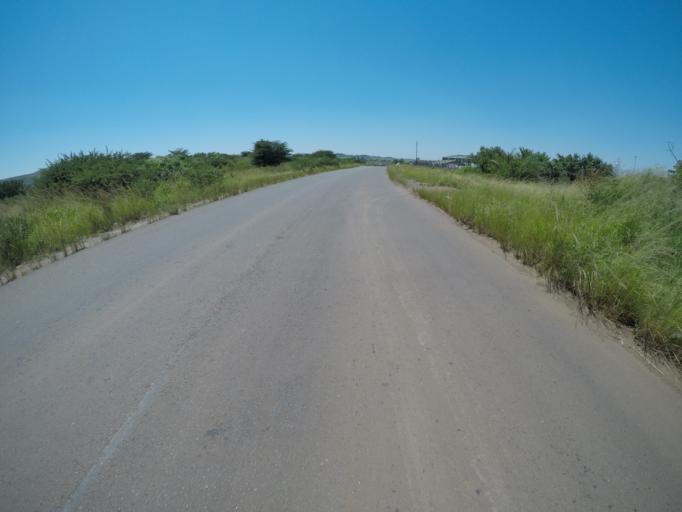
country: ZA
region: KwaZulu-Natal
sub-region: uThungulu District Municipality
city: Empangeni
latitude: -28.7217
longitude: 31.8675
